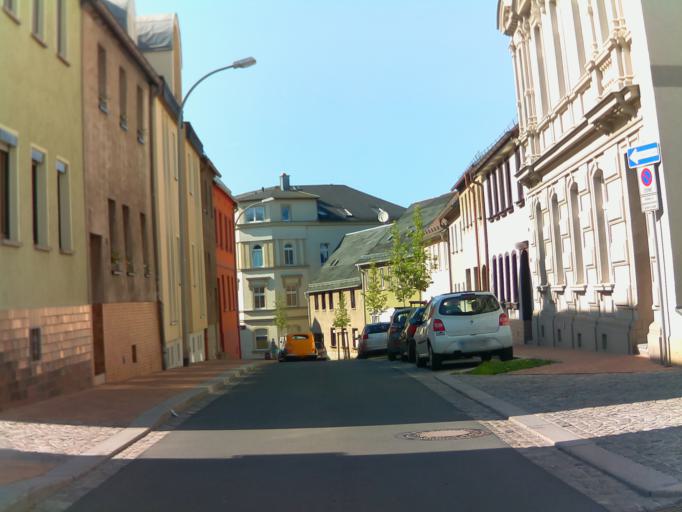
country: DE
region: Thuringia
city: Zeulenroda
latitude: 50.6501
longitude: 11.9790
